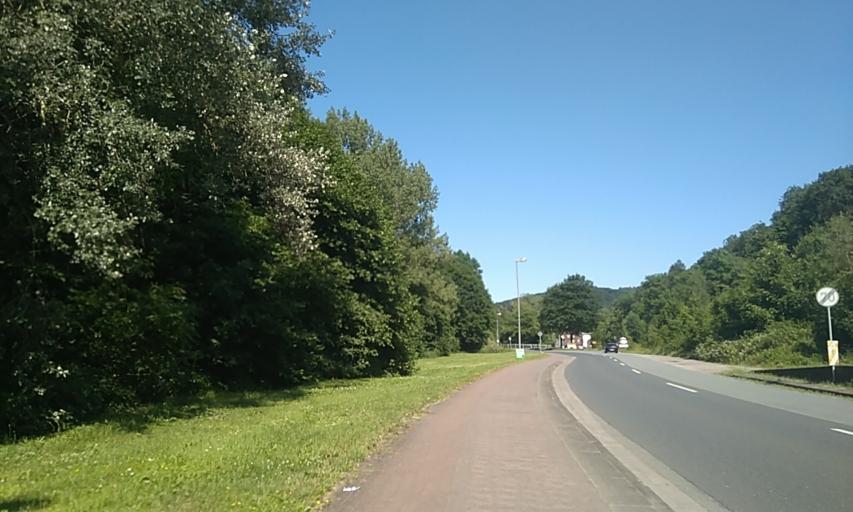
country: DE
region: Lower Saxony
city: Bodenwerder
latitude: 51.9823
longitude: 9.5282
